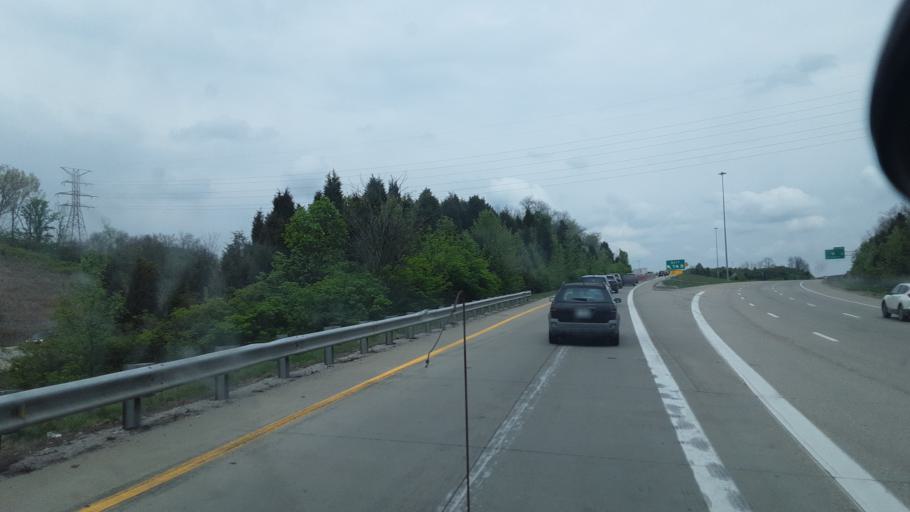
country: US
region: Kentucky
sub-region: Campbell County
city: Highland Heights
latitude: 39.0447
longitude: -84.4673
